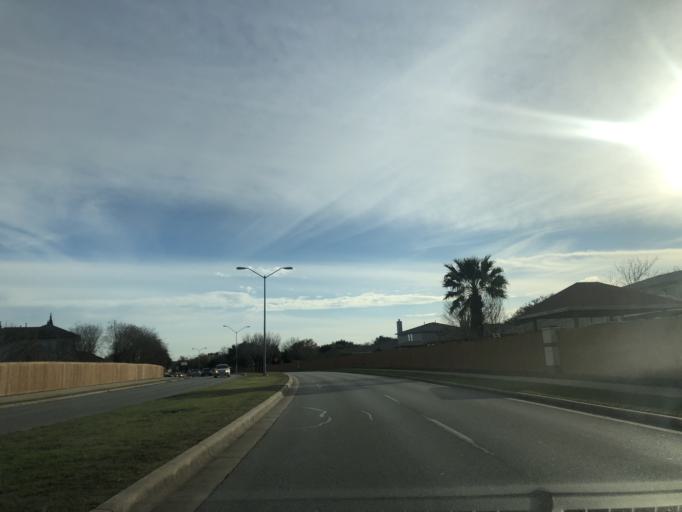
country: US
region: Texas
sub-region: Travis County
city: Windemere
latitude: 30.4627
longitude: -97.6344
